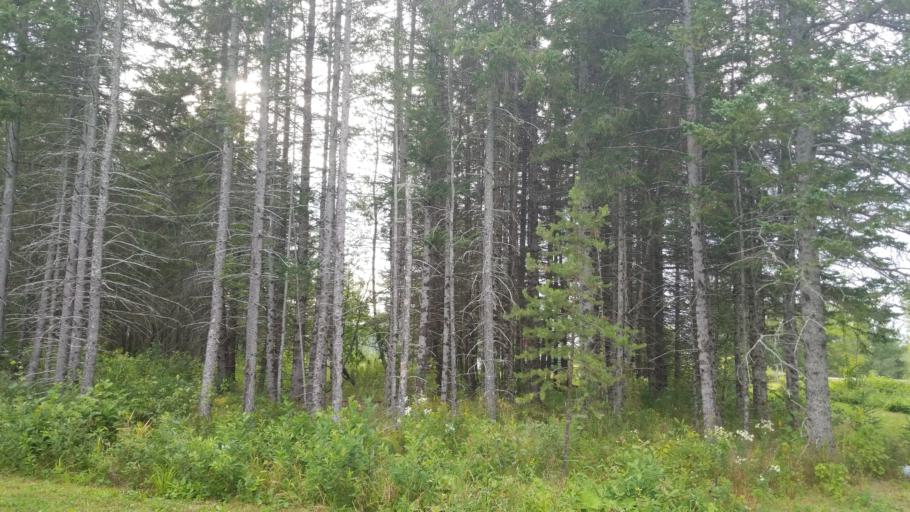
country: CA
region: New Brunswick
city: Salisbury
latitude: 45.9952
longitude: -65.1516
